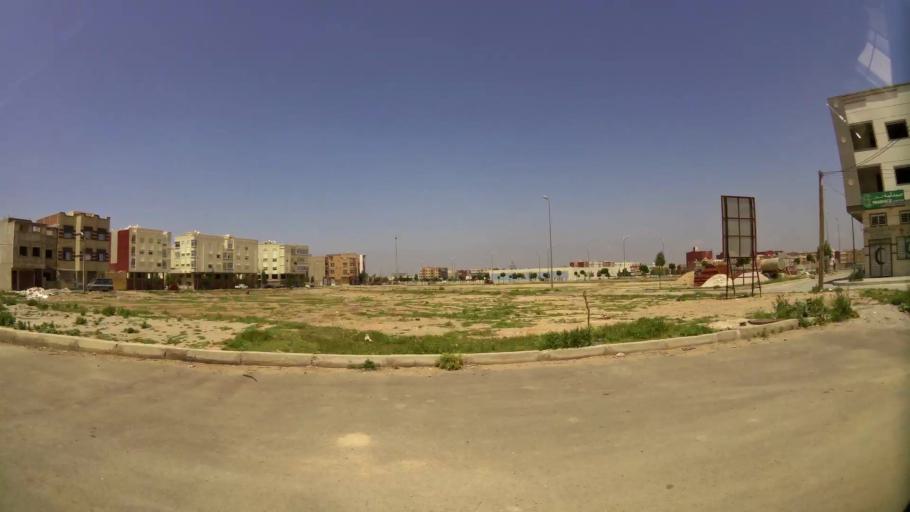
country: MA
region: Oriental
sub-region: Oujda-Angad
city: Oujda
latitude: 34.6951
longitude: -1.8935
